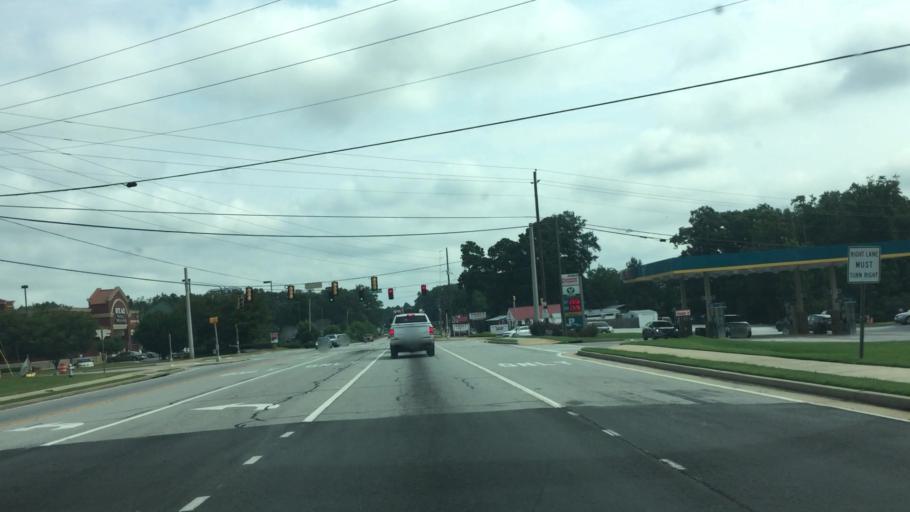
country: US
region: Georgia
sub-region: Henry County
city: McDonough
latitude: 33.5068
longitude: -84.1410
